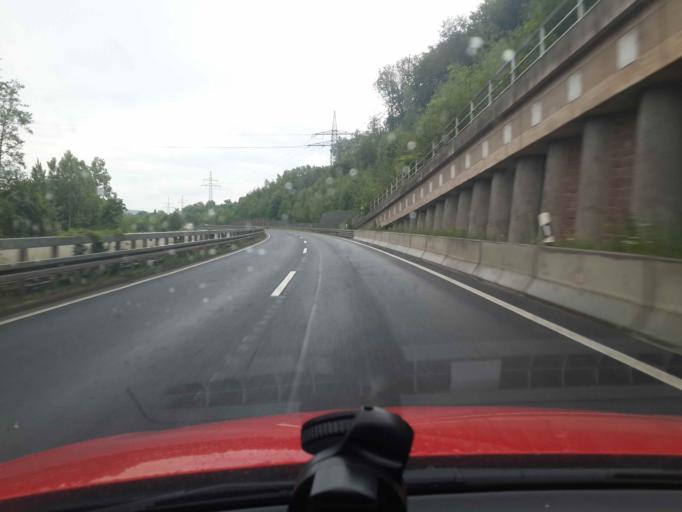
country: DE
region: Bavaria
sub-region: Regierungsbezirk Unterfranken
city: Worth am Main
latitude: 49.8087
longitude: 9.1347
